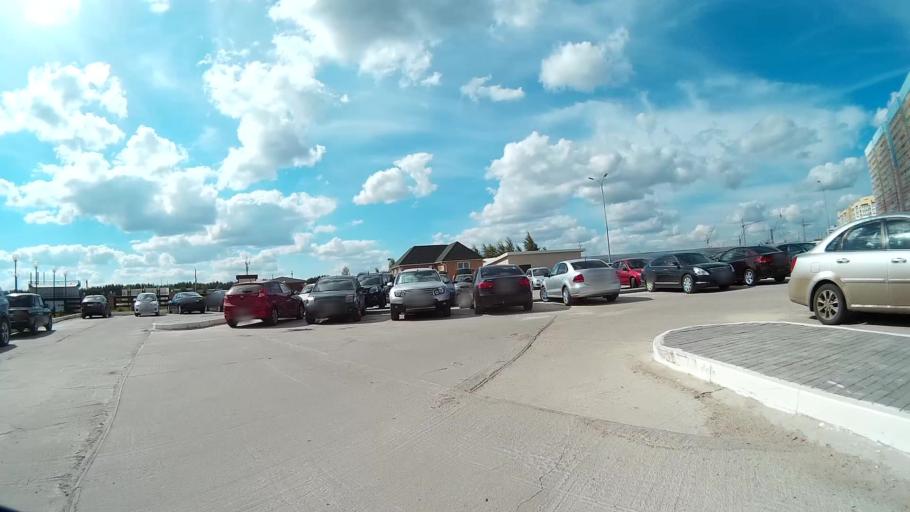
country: RU
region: Ulyanovsk
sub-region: Ulyanovskiy Rayon
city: Ulyanovsk
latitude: 54.2753
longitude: 48.2667
